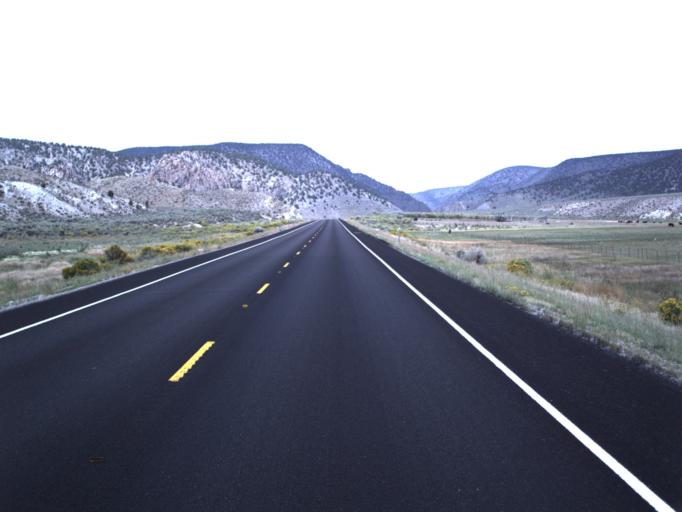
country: US
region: Utah
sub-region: Garfield County
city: Panguitch
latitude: 38.0404
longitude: -112.3550
